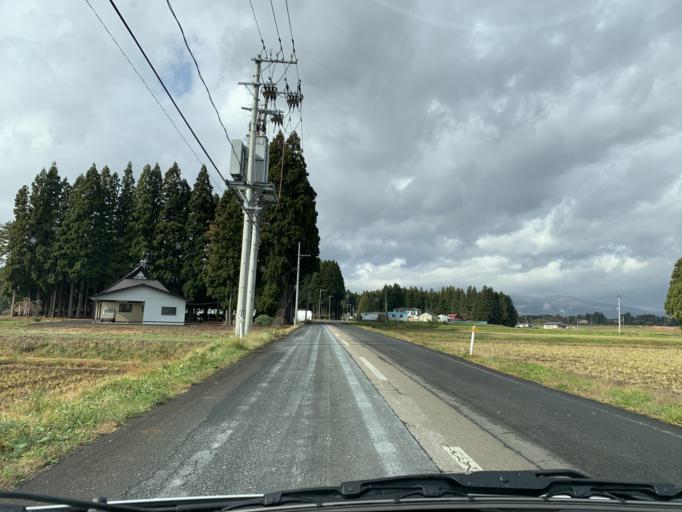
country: JP
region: Iwate
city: Mizusawa
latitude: 39.0868
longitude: 141.0234
